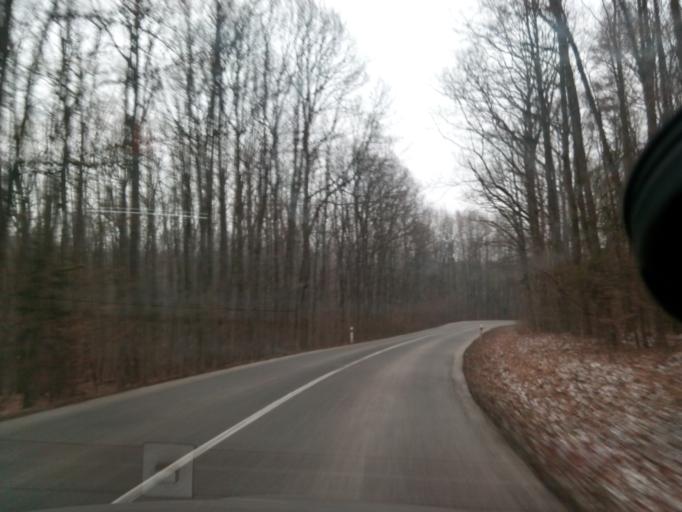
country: SK
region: Kosicky
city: Moldava nad Bodvou
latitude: 48.6902
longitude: 21.0345
